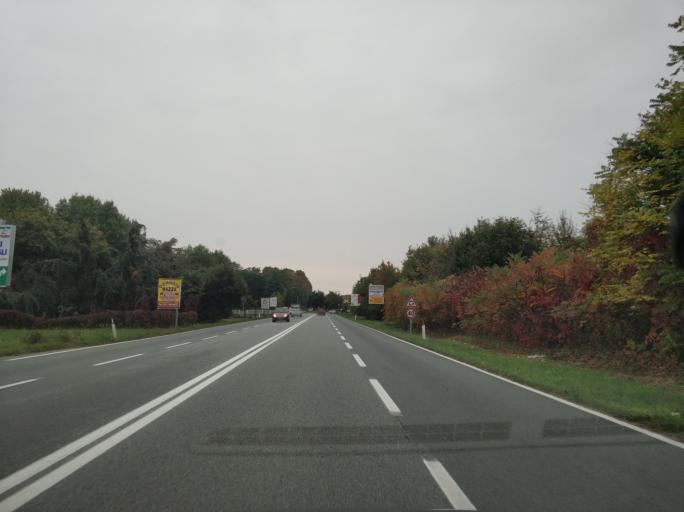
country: IT
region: Piedmont
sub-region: Provincia di Torino
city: San Maurizio
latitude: 45.2073
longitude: 7.6179
